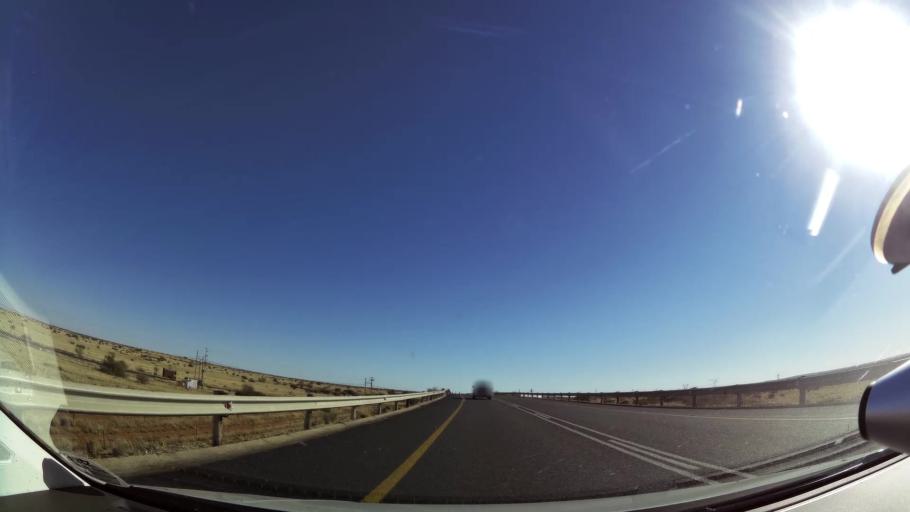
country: ZA
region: Northern Cape
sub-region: Frances Baard District Municipality
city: Kimberley
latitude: -28.4603
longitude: 24.7941
